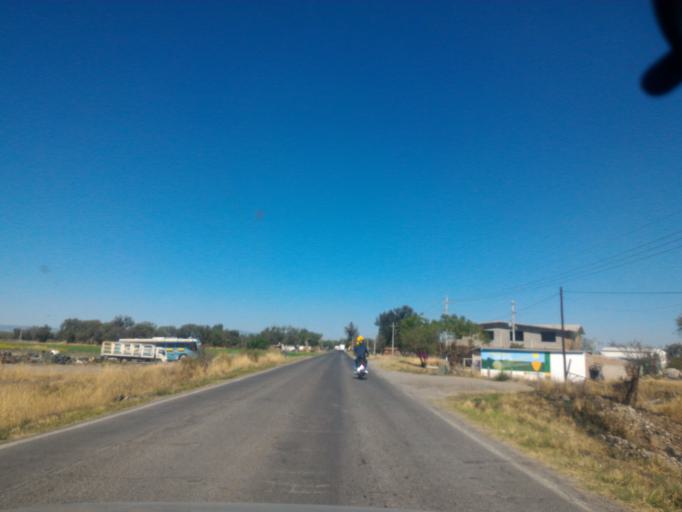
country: MX
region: Guanajuato
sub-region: San Francisco del Rincon
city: San Roque de Montes
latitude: 20.9985
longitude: -101.8103
